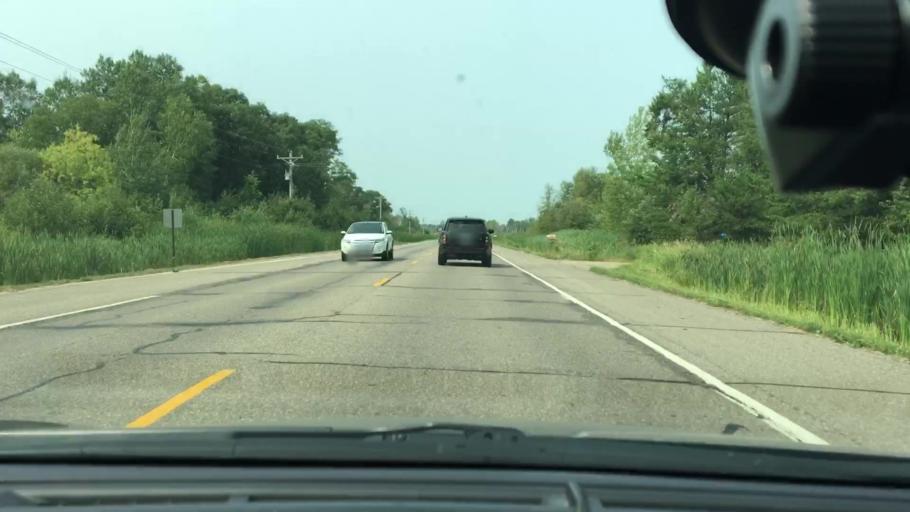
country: US
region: Minnesota
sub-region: Crow Wing County
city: Brainerd
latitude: 46.3985
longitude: -94.2136
